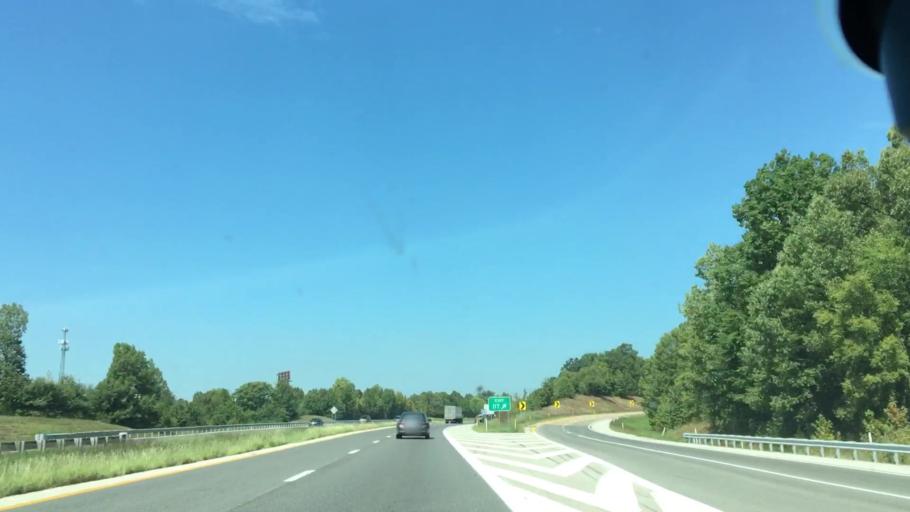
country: US
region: Kentucky
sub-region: Hopkins County
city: Madisonville
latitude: 37.3581
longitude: -87.4894
